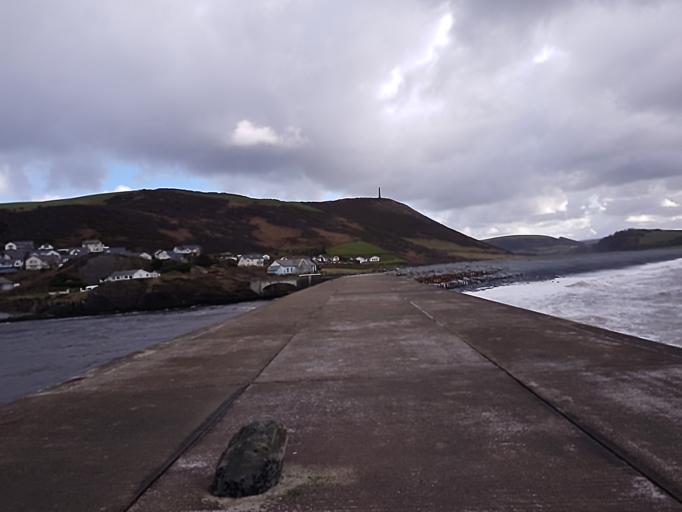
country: GB
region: Wales
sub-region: County of Ceredigion
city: Aberystwyth
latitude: 52.4067
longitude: -4.0918
